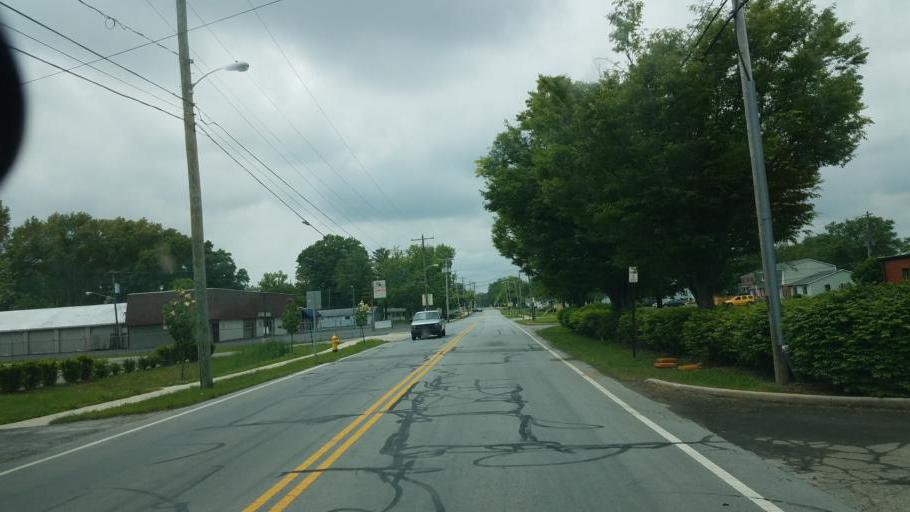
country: US
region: Ohio
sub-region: Delaware County
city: Delaware
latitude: 40.3135
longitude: -83.0824
